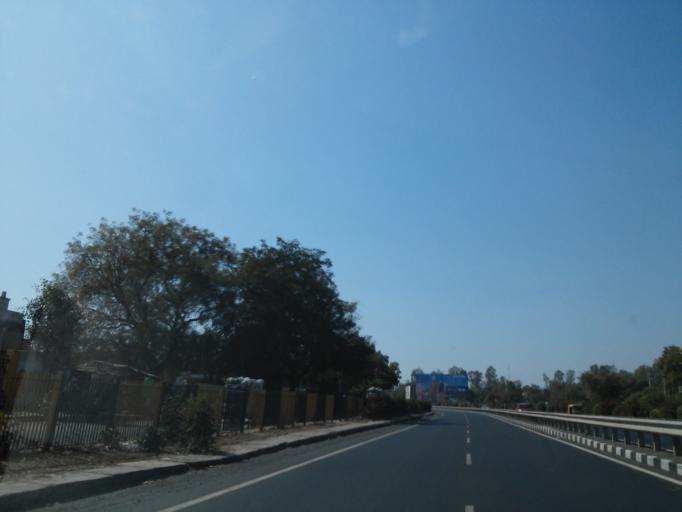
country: IN
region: Gujarat
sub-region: Gandhinagar
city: Chhala
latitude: 23.4431
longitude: 72.8476
